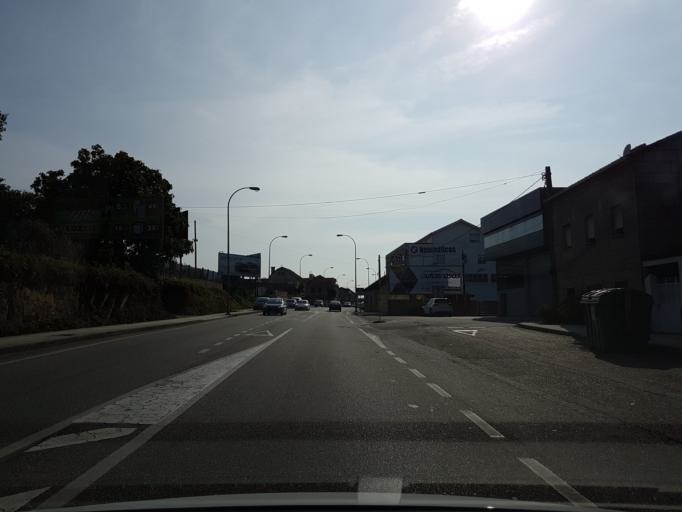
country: ES
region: Galicia
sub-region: Provincia de Pontevedra
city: Vigo
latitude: 42.2015
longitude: -8.7558
